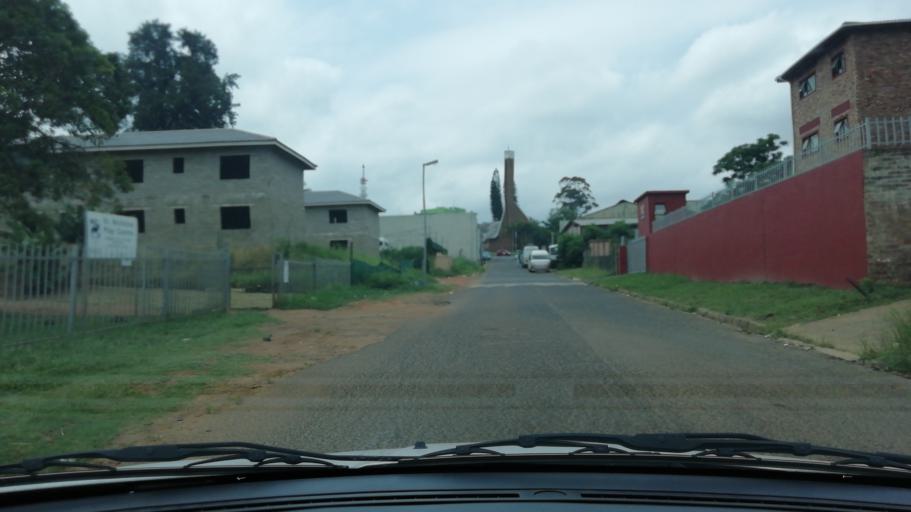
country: ZA
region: KwaZulu-Natal
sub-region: uThungulu District Municipality
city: Empangeni
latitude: -28.7479
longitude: 31.8910
